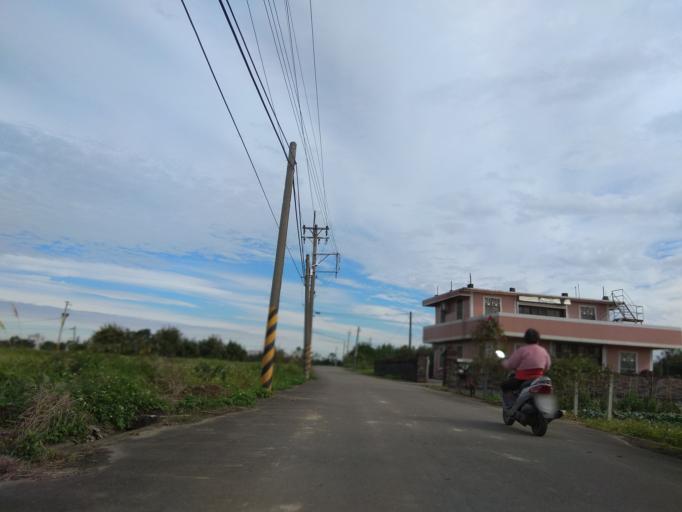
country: TW
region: Taiwan
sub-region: Hsinchu
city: Zhubei
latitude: 24.9491
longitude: 121.1092
